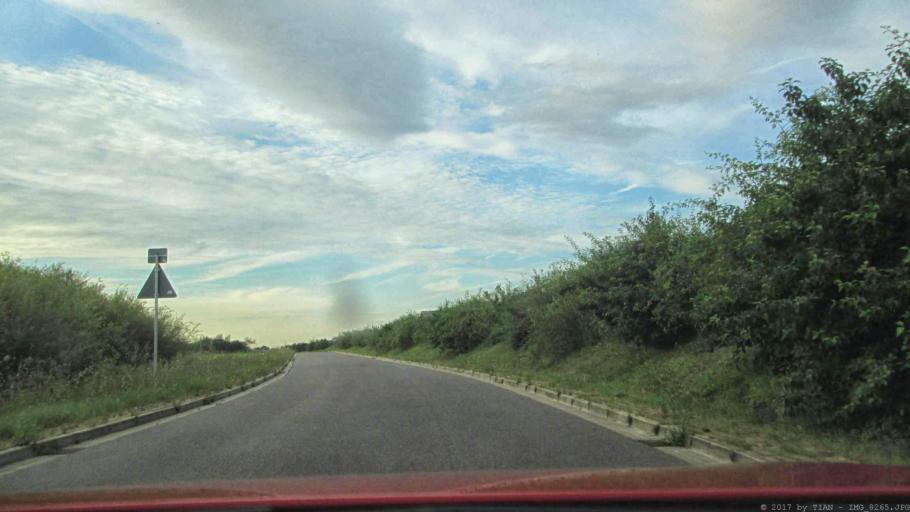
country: DE
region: Lower Saxony
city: Weyhausen
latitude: 52.3999
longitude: 10.7153
